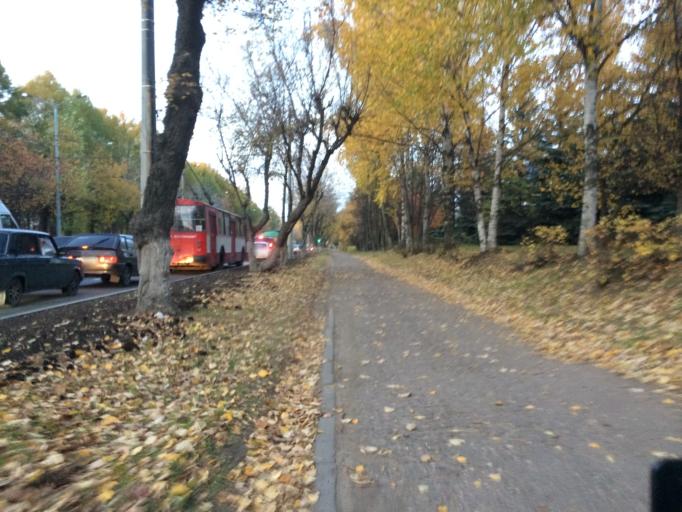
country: RU
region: Mariy-El
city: Yoshkar-Ola
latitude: 56.6119
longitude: 47.8808
